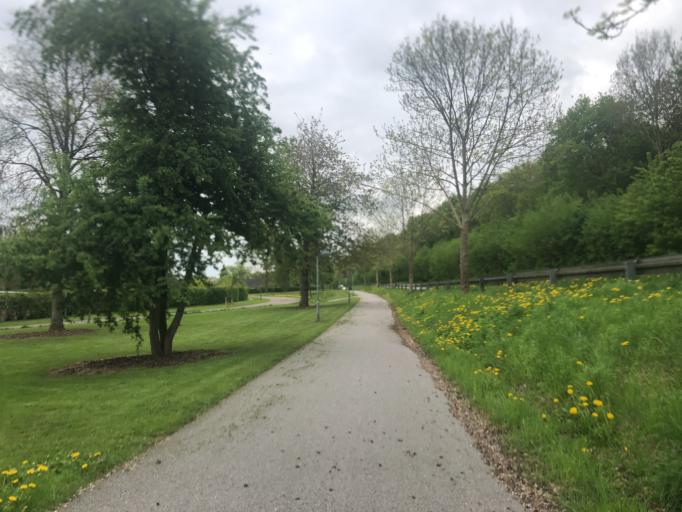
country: DK
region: Zealand
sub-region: Koge Kommune
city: Bjaeverskov
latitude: 55.4553
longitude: 12.0306
